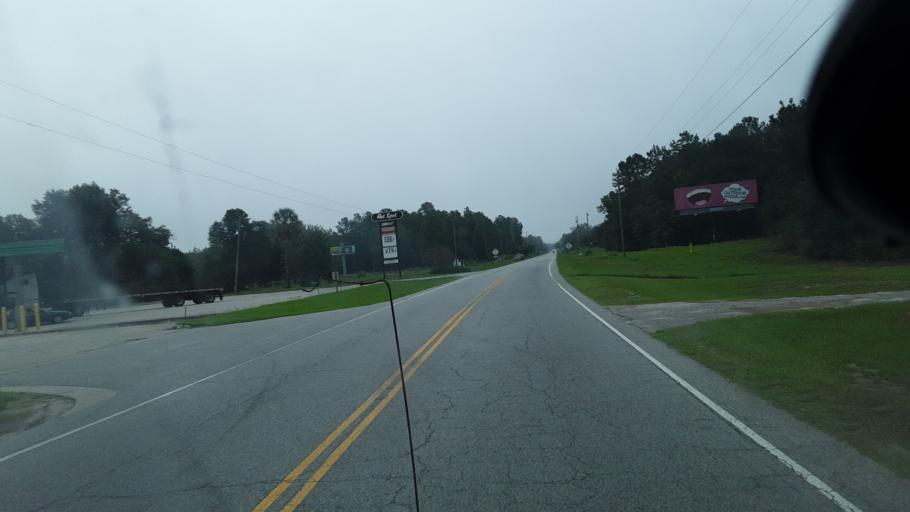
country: US
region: South Carolina
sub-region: Florence County
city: Johnsonville
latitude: 33.9115
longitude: -79.4065
